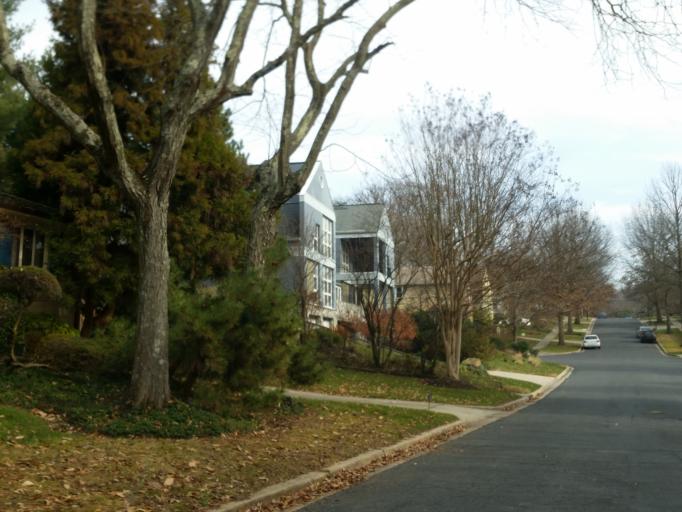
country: US
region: Maryland
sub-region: Montgomery County
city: Forest Glen
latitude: 38.9903
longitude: -77.0558
